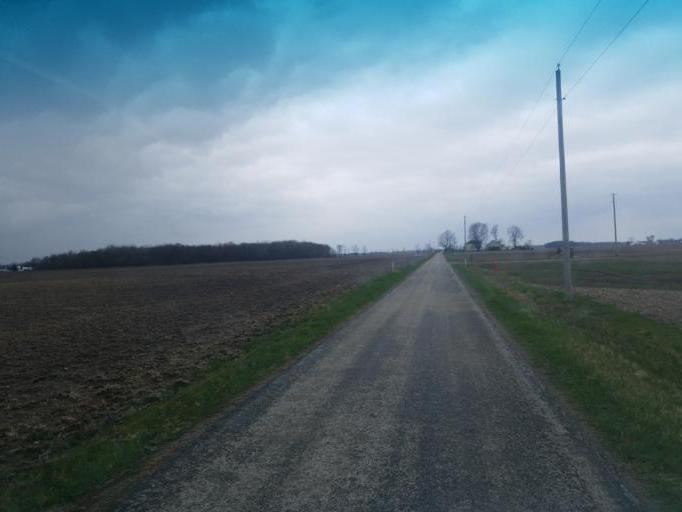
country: US
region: Ohio
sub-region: Marion County
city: Prospect
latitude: 40.4394
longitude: -83.1298
